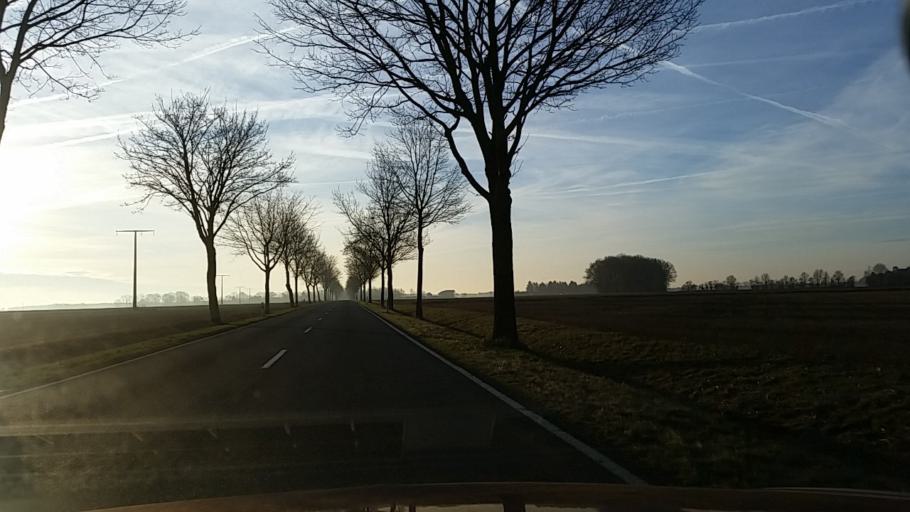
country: DE
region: Lower Saxony
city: Sprakensehl
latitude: 52.7597
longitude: 10.5044
